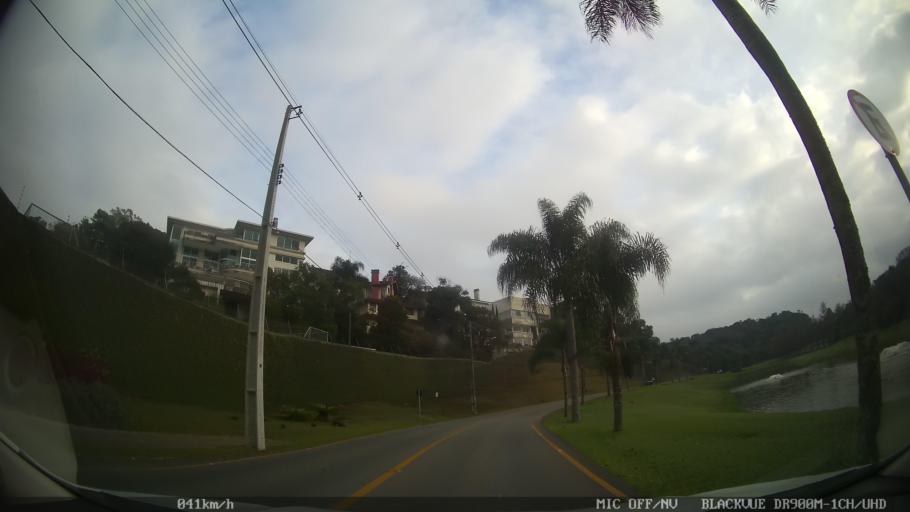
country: BR
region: Parana
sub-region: Curitiba
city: Curitiba
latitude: -25.3975
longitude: -49.3061
